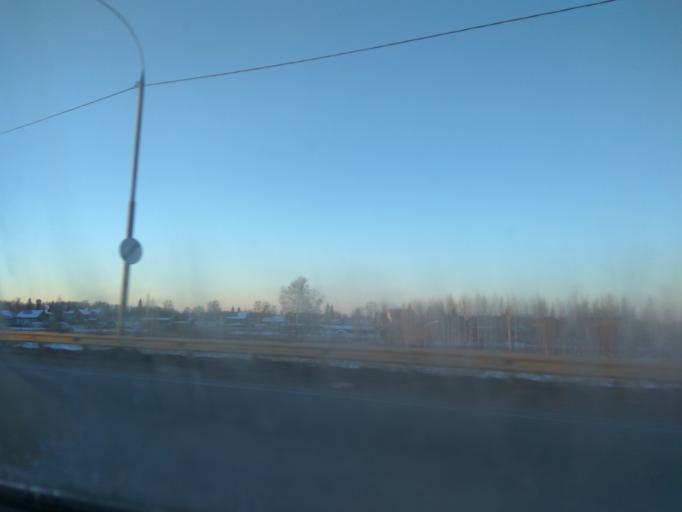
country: RU
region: Novosibirsk
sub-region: Novosibirskiy Rayon
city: Novosibirsk
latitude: 55.1333
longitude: 82.9746
